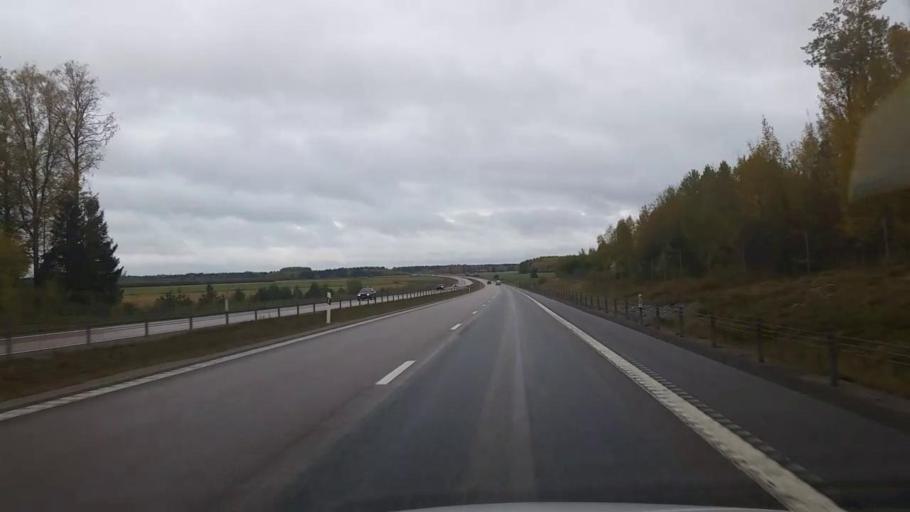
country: SE
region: Uppsala
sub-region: Osthammars Kommun
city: Bjorklinge
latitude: 60.1382
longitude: 17.5468
